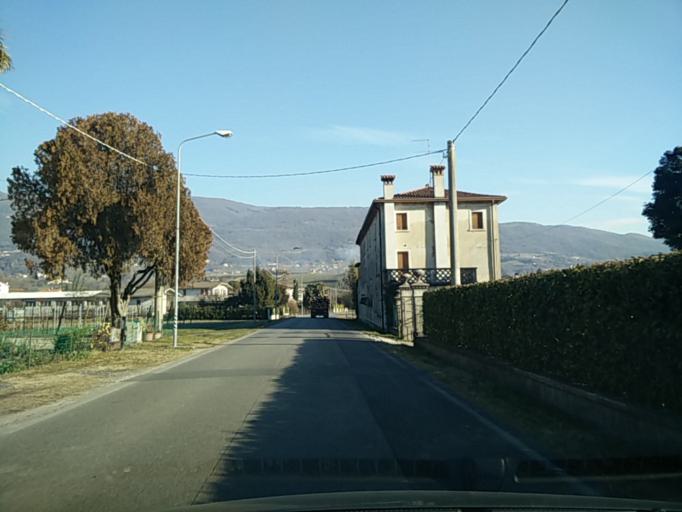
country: IT
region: Veneto
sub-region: Provincia di Treviso
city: Cappella Maggiore
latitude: 45.9735
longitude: 12.3719
